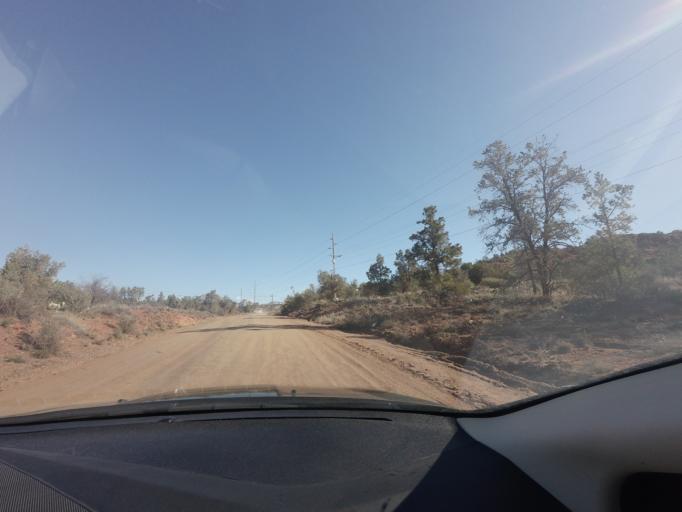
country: US
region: Arizona
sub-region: Yavapai County
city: West Sedona
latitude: 34.8202
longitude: -111.8085
